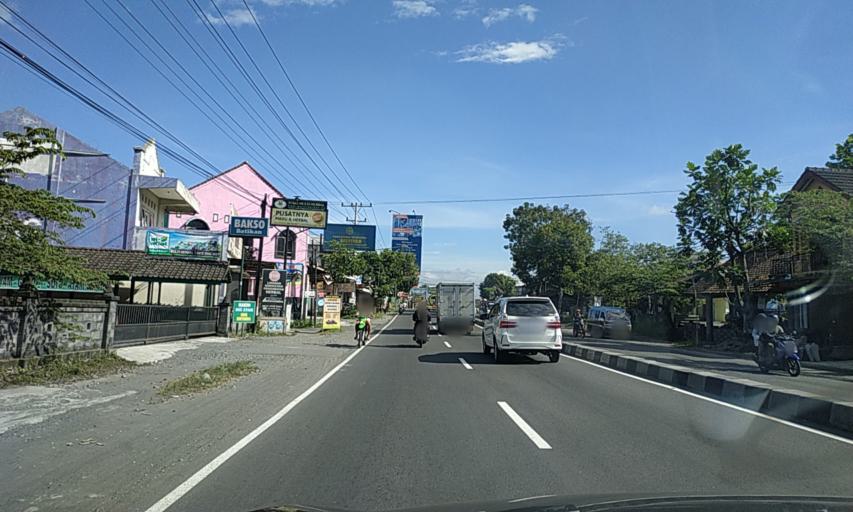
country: ID
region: Central Java
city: Muntilan
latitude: -7.5725
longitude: 110.2611
